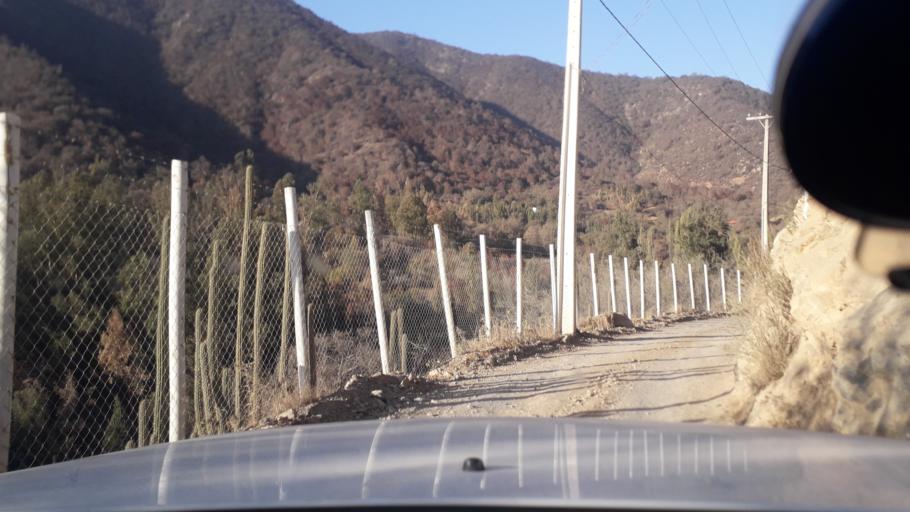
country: CL
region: Valparaiso
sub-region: Provincia de Marga Marga
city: Limache
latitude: -33.0516
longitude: -71.0866
